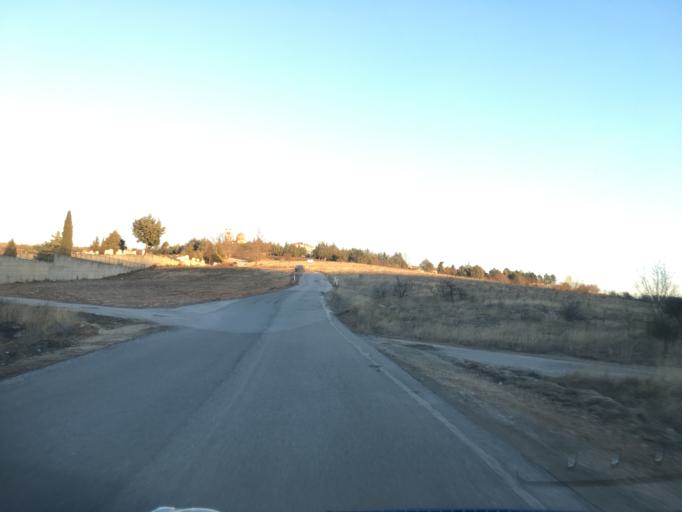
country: GR
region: West Macedonia
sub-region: Nomos Kozanis
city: Koila
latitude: 40.3226
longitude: 21.8154
